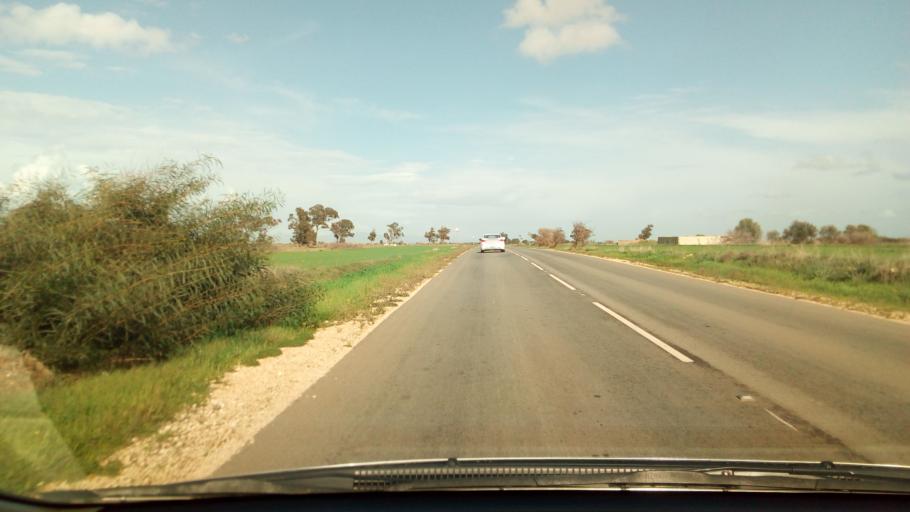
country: CY
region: Ammochostos
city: Achna
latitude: 35.0567
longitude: 33.7956
